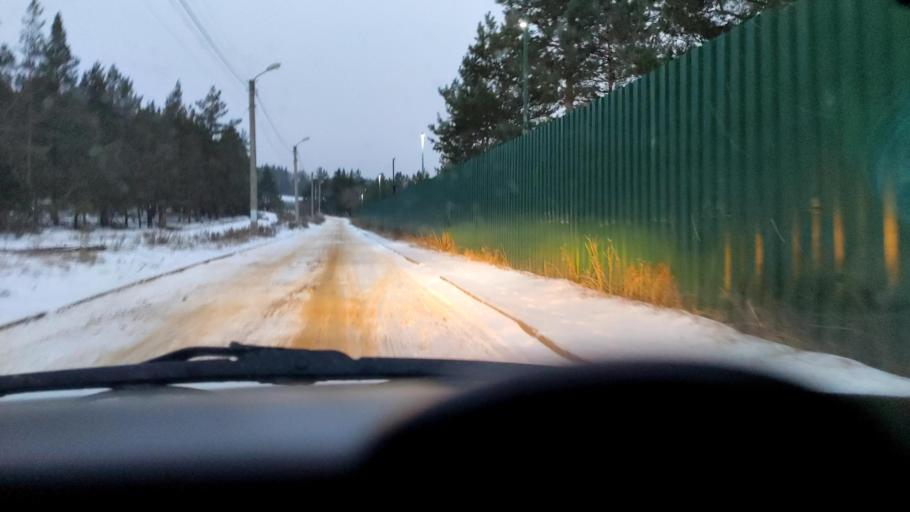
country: RU
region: Voronezj
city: Pridonskoy
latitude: 51.7050
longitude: 39.1070
